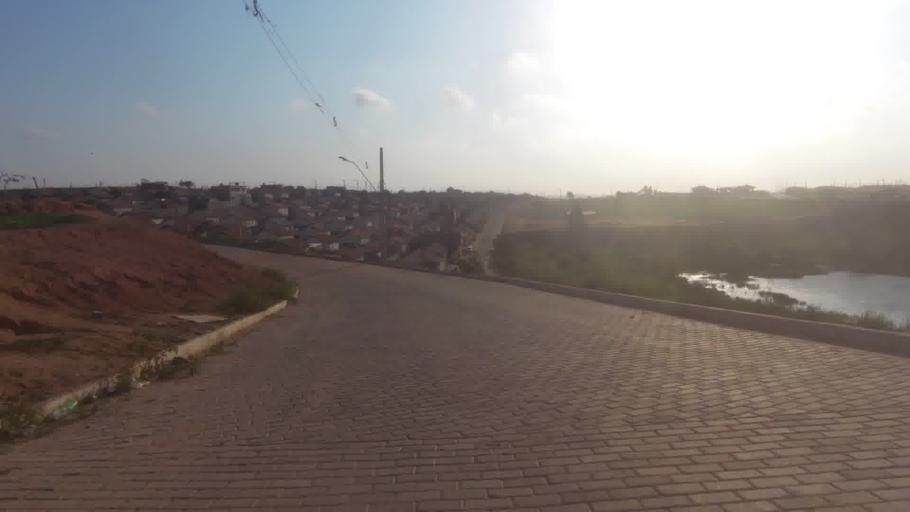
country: BR
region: Espirito Santo
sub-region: Itapemirim
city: Itapemirim
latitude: -21.0183
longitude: -40.8317
